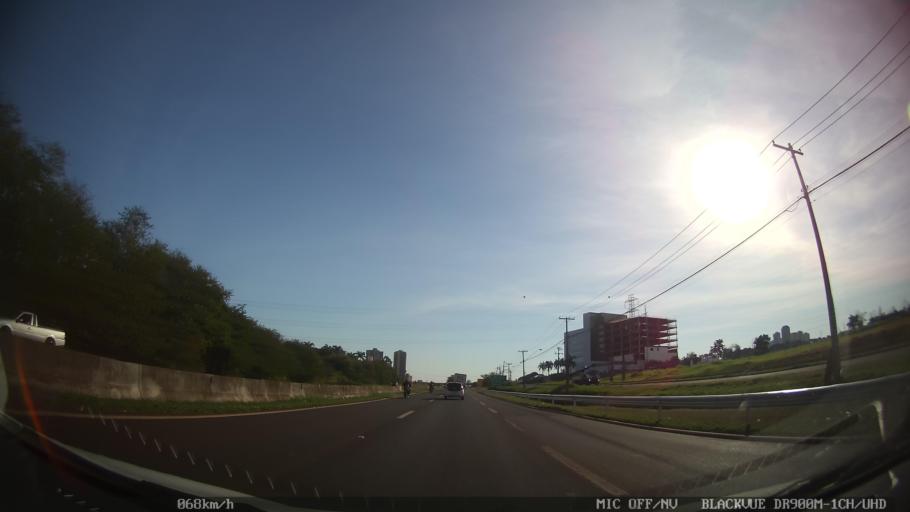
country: BR
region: Sao Paulo
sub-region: Ribeirao Preto
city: Ribeirao Preto
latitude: -21.2282
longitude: -47.8175
